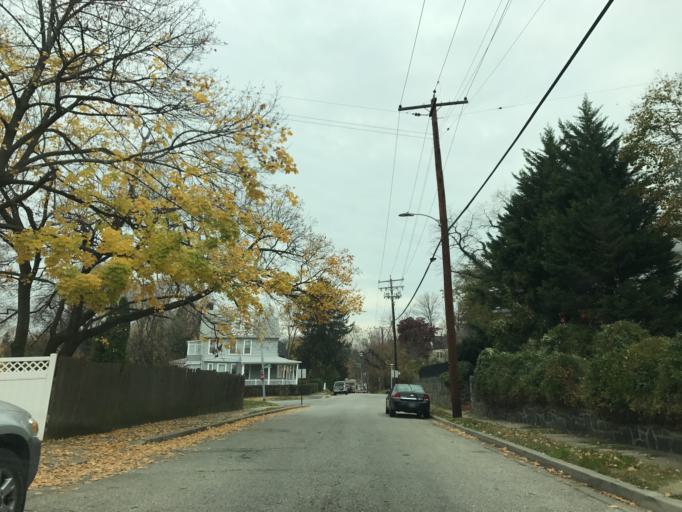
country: US
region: Maryland
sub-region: Baltimore County
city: Woodlawn
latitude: 39.3119
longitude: -76.6774
